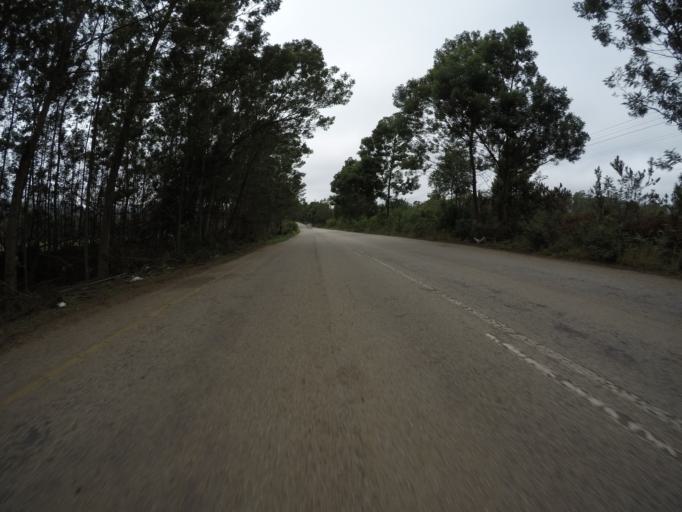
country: ZA
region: Eastern Cape
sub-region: Cacadu District Municipality
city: Kareedouw
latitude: -33.9969
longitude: 24.1518
